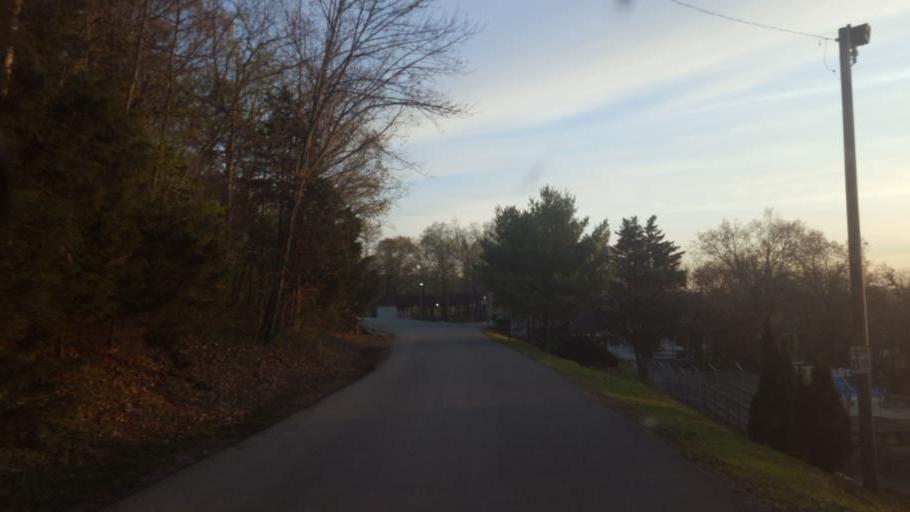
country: US
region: Kentucky
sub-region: Barren County
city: Cave City
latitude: 37.1368
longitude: -85.9962
